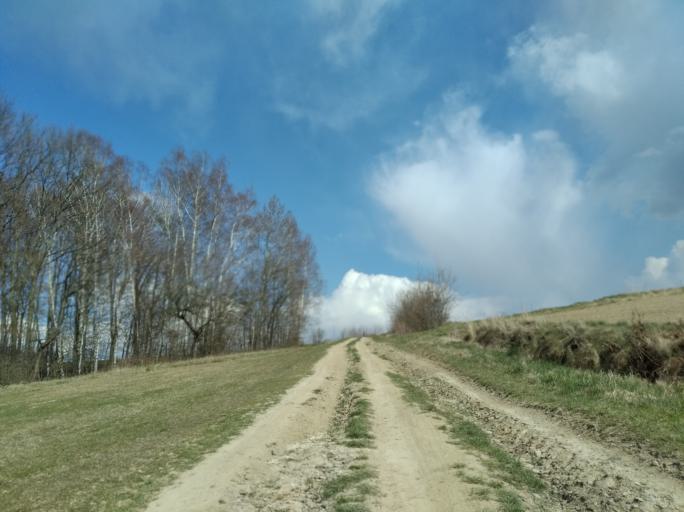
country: PL
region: Subcarpathian Voivodeship
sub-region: Powiat strzyzowski
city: Strzyzow
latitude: 49.9227
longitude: 21.7309
